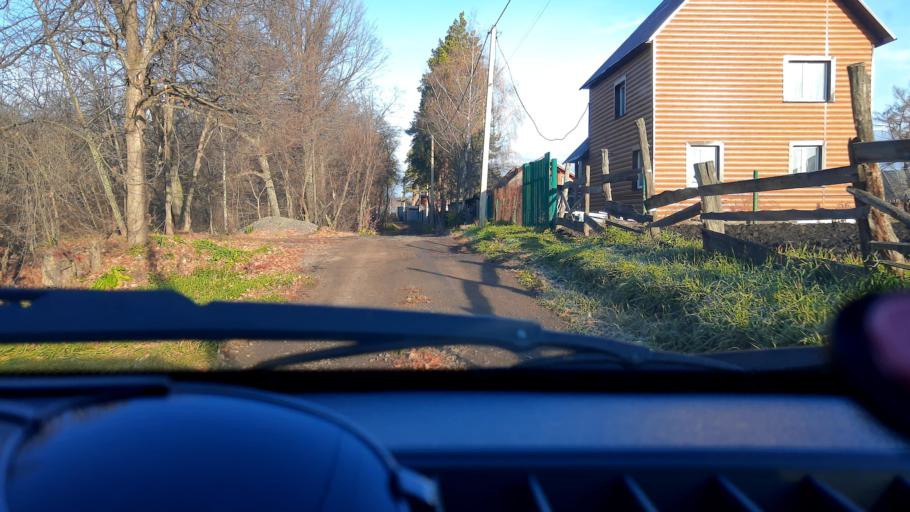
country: RU
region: Bashkortostan
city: Ufa
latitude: 54.7877
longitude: 55.9438
